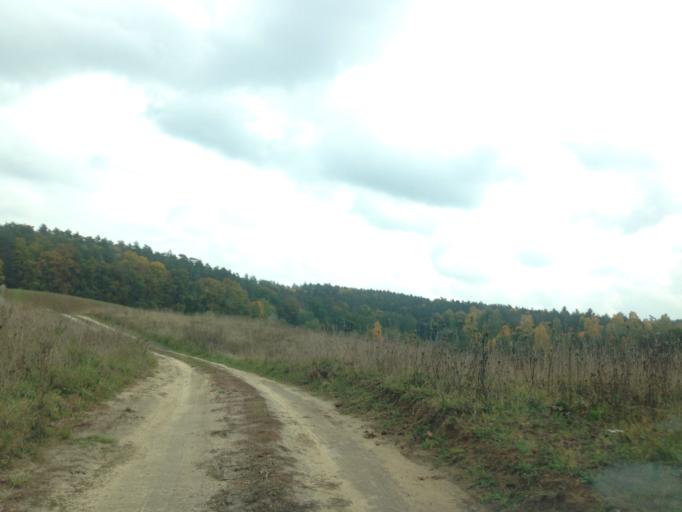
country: PL
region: Kujawsko-Pomorskie
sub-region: Powiat brodnicki
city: Gorzno
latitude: 53.2544
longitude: 19.6850
